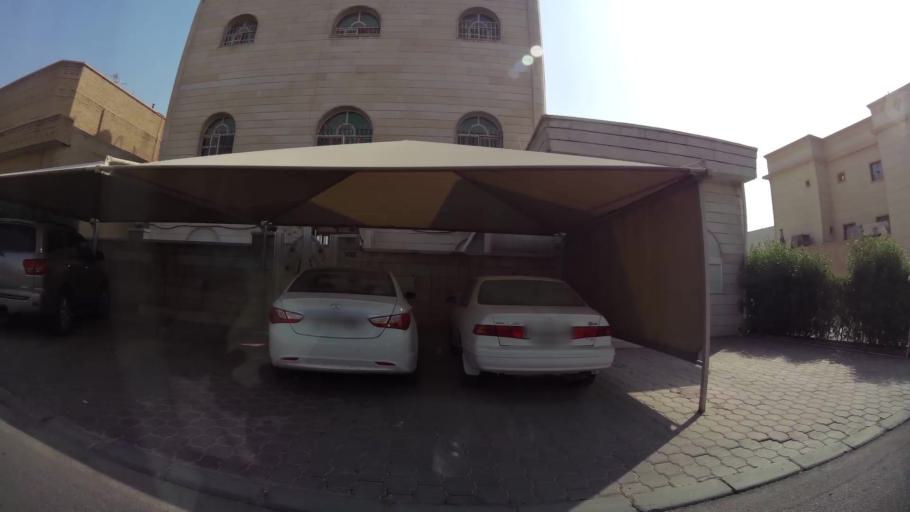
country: KW
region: Al Asimah
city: Ar Rabiyah
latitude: 29.2698
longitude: 47.8698
